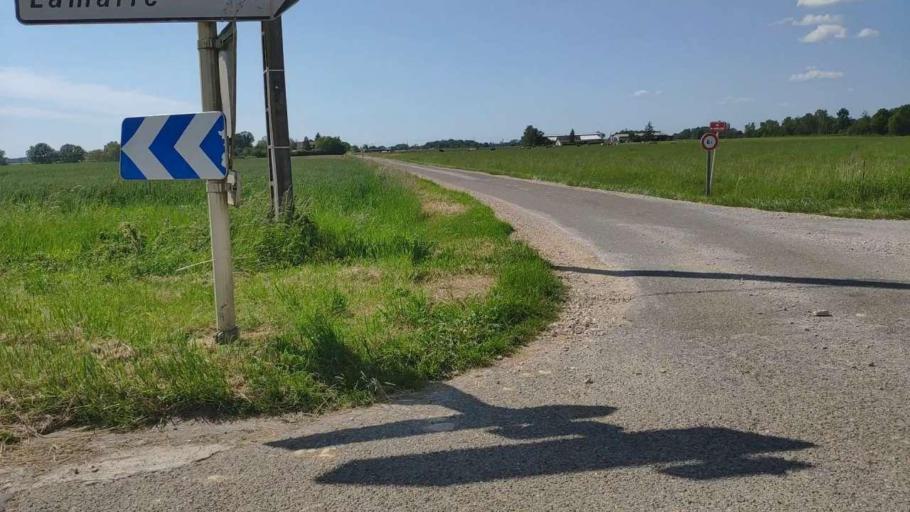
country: FR
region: Franche-Comte
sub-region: Departement du Jura
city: Bletterans
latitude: 46.8120
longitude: 5.3974
